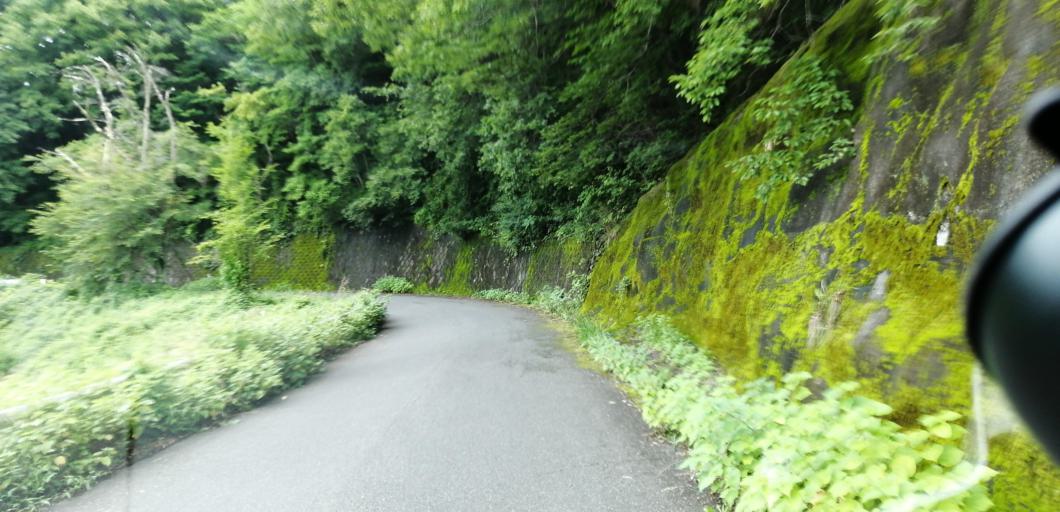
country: JP
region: Saitama
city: Chichibu
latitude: 36.0371
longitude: 139.1145
